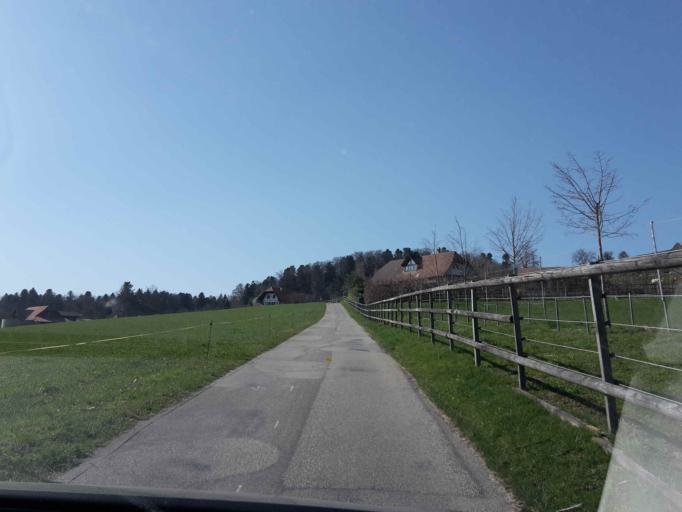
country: CH
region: Bern
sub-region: Oberaargau
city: Herzogenbuchsee
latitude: 47.1909
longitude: 7.7471
